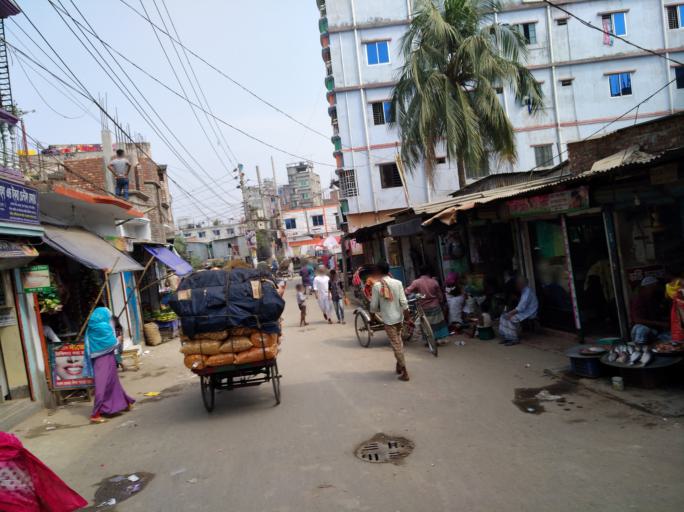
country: BD
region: Dhaka
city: Azimpur
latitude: 23.7157
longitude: 90.3759
